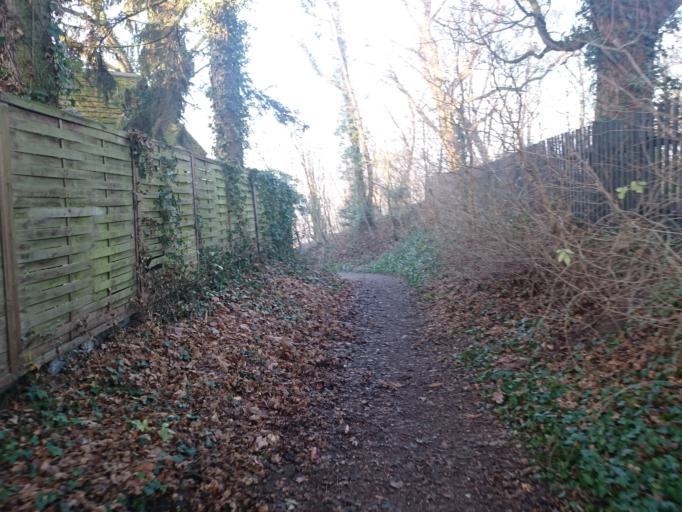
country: AT
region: Upper Austria
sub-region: Linz Stadt
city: Linz
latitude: 48.2973
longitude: 14.2803
